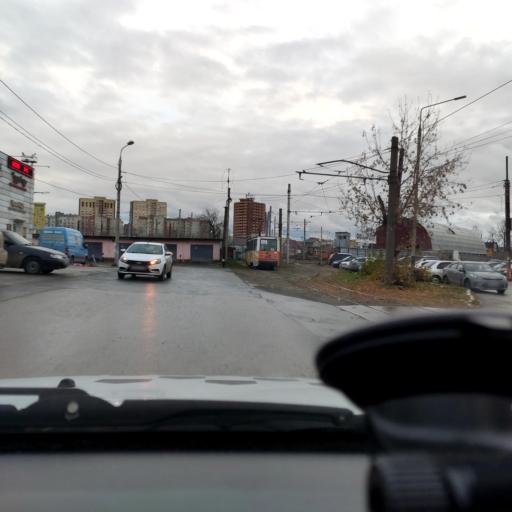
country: RU
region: Perm
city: Perm
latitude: 57.9778
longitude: 56.1906
